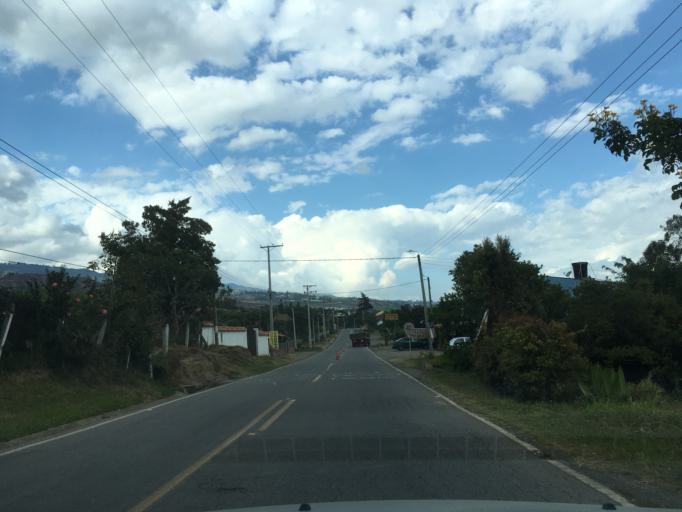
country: CO
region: Boyaca
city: Sutamarchan
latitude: 5.5942
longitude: -73.6391
